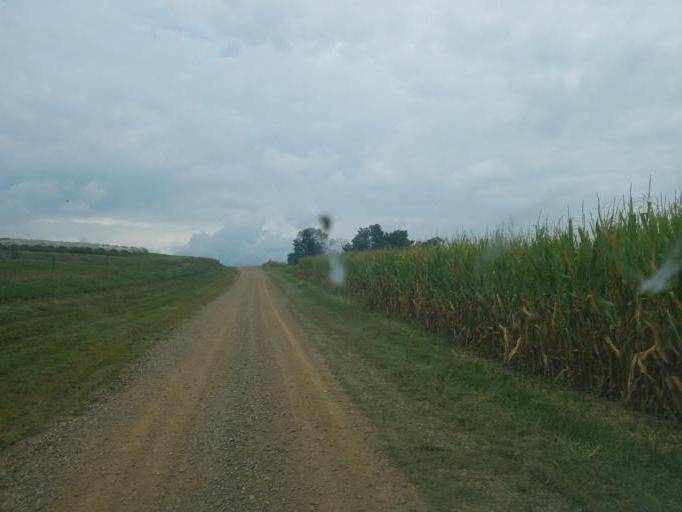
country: US
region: Ohio
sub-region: Knox County
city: Danville
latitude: 40.5201
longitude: -82.3052
